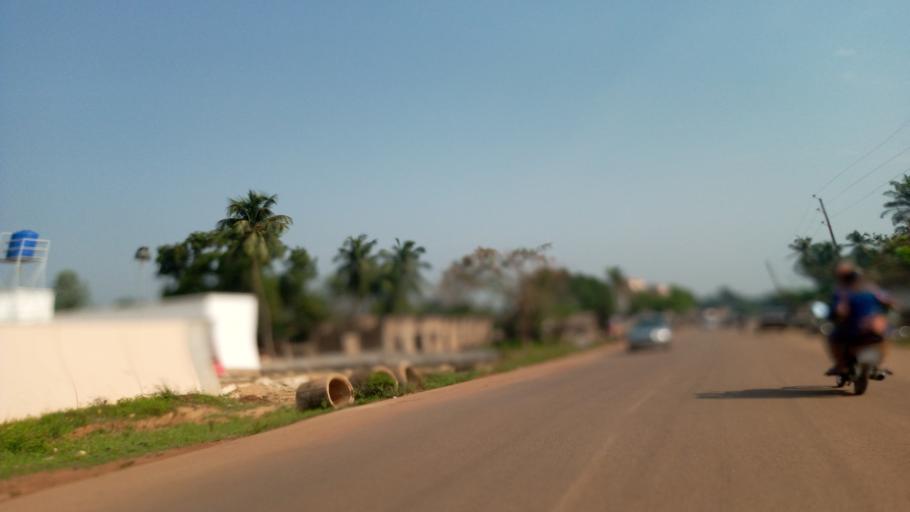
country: BJ
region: Queme
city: Porto-Novo
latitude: 6.5365
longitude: 2.6487
